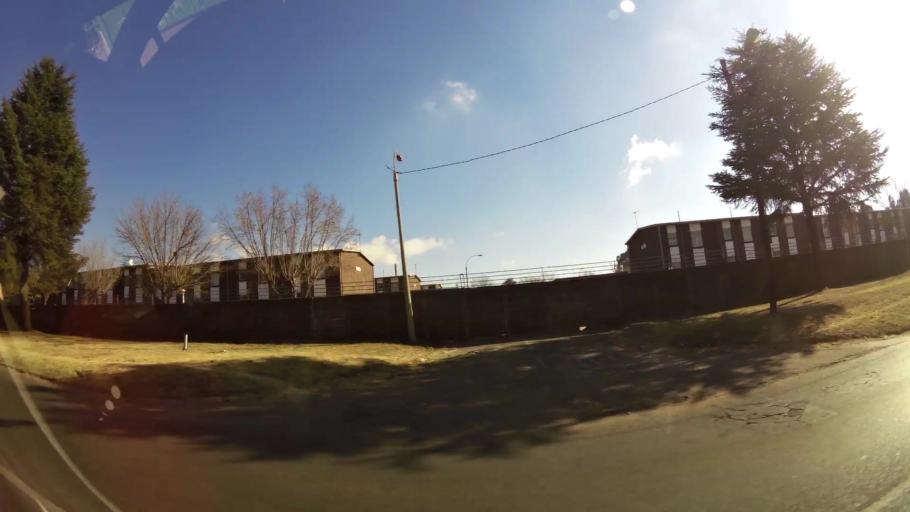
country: ZA
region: Gauteng
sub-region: City of Johannesburg Metropolitan Municipality
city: Roodepoort
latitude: -26.1522
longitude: 27.8353
